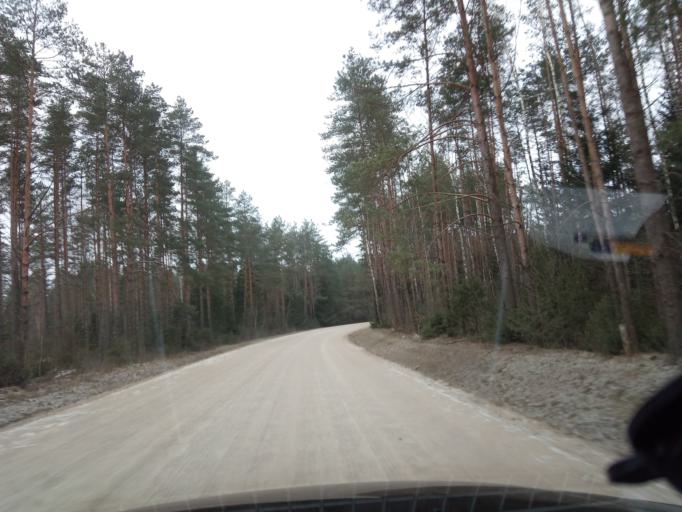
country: LT
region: Alytaus apskritis
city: Varena
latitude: 54.1215
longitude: 24.6310
